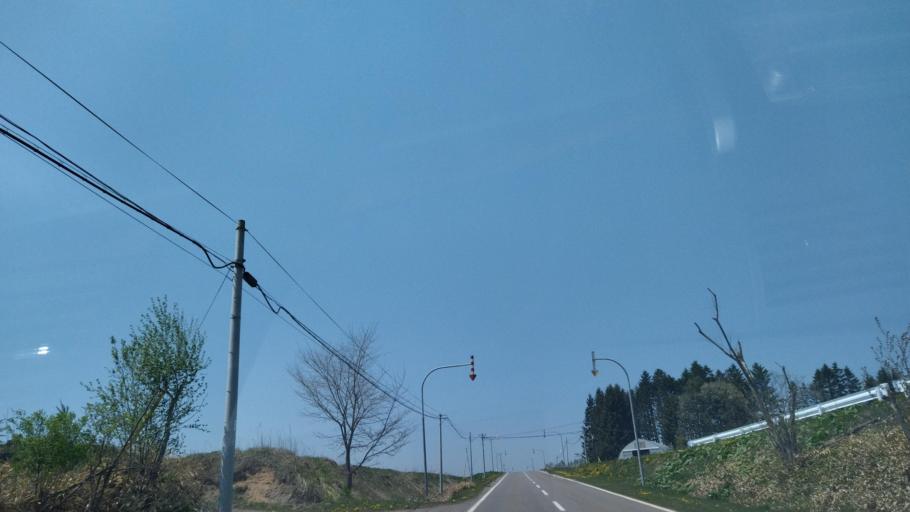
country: JP
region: Hokkaido
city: Obihiro
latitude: 42.9040
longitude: 143.0025
